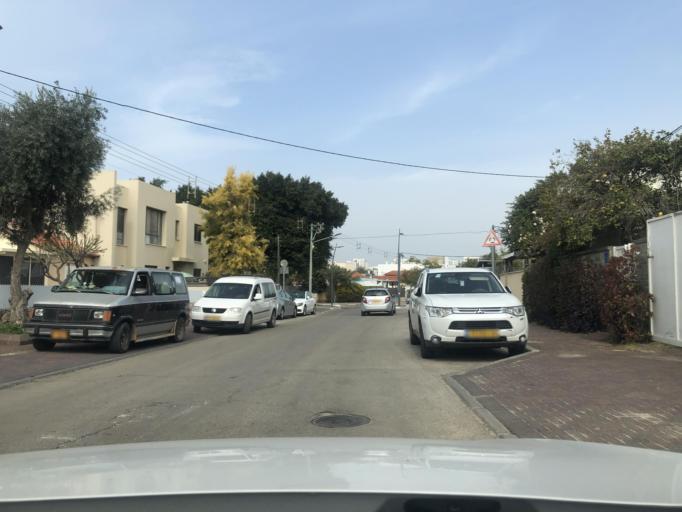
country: IL
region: Central District
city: Rosh Ha'Ayin
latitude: 32.0957
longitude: 34.9487
